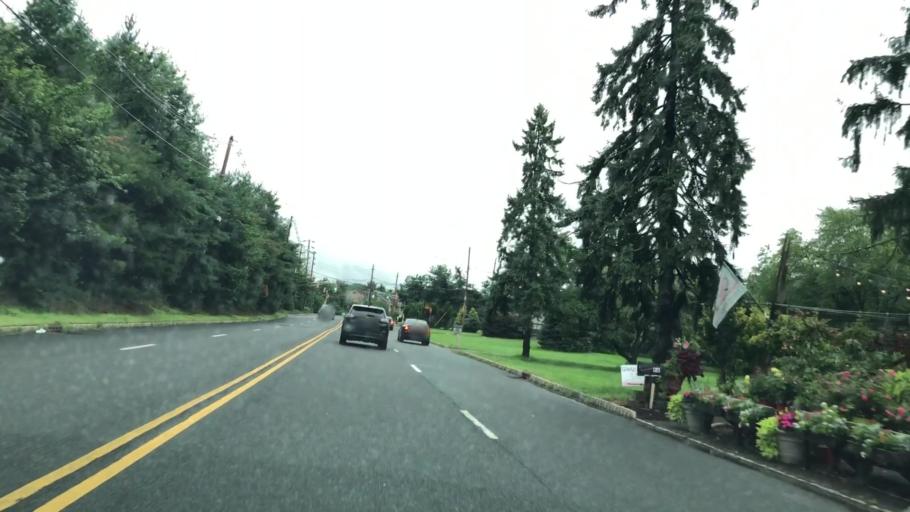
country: US
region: New Jersey
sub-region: Morris County
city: Hanover
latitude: 40.8077
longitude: -74.3619
